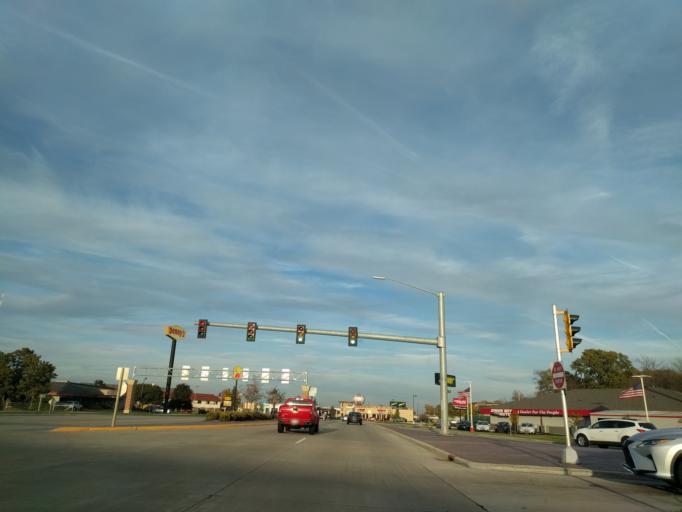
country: US
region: Wisconsin
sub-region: Brown County
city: Ashwaubenon
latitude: 44.4698
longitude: -88.0785
